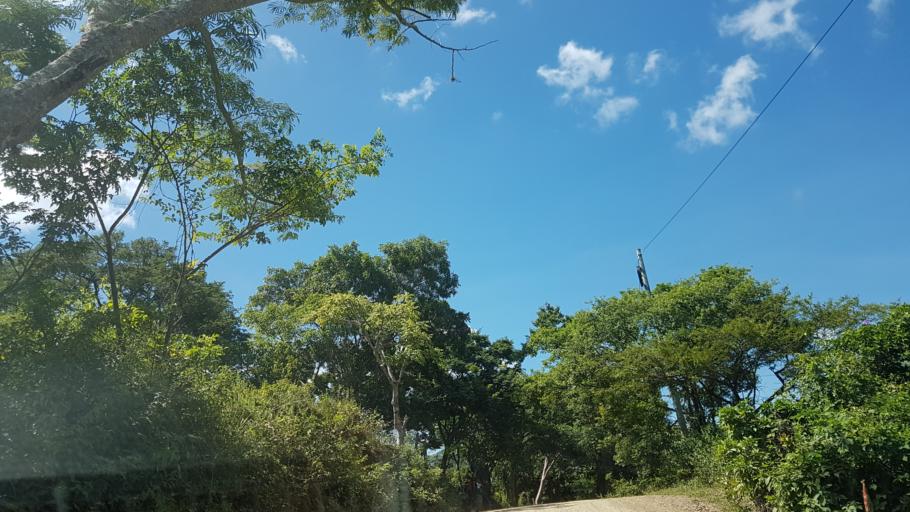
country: HN
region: El Paraiso
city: Santa Cruz
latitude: 13.7327
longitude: -86.6920
